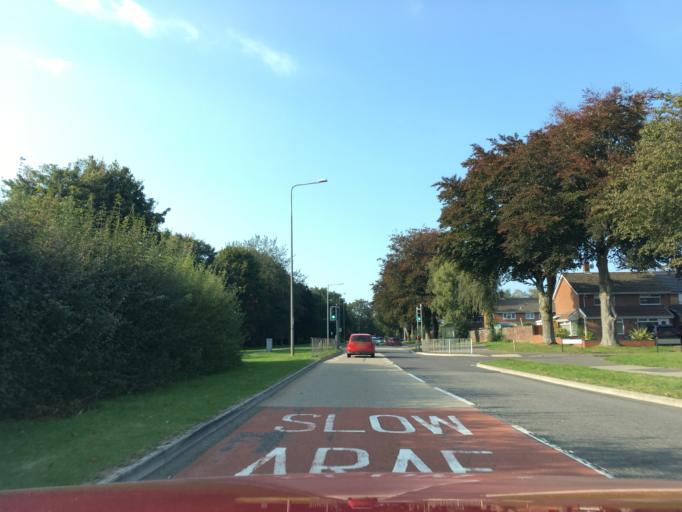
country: GB
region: Wales
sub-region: Torfaen County Borough
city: Cwmbran
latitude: 51.6418
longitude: -3.0053
